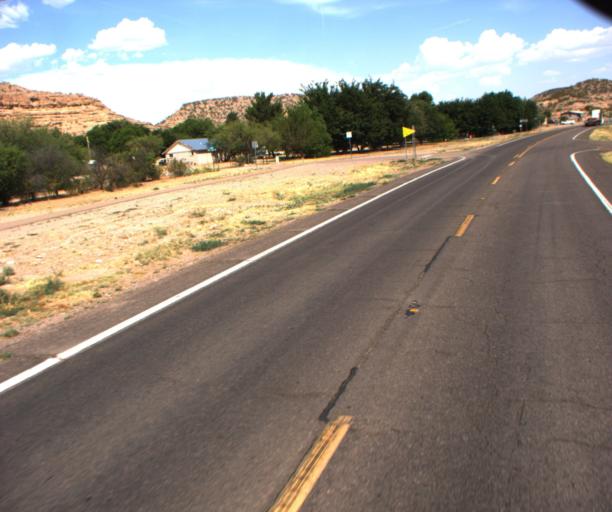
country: US
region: Arizona
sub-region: Greenlee County
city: Clifton
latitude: 32.9279
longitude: -109.2024
